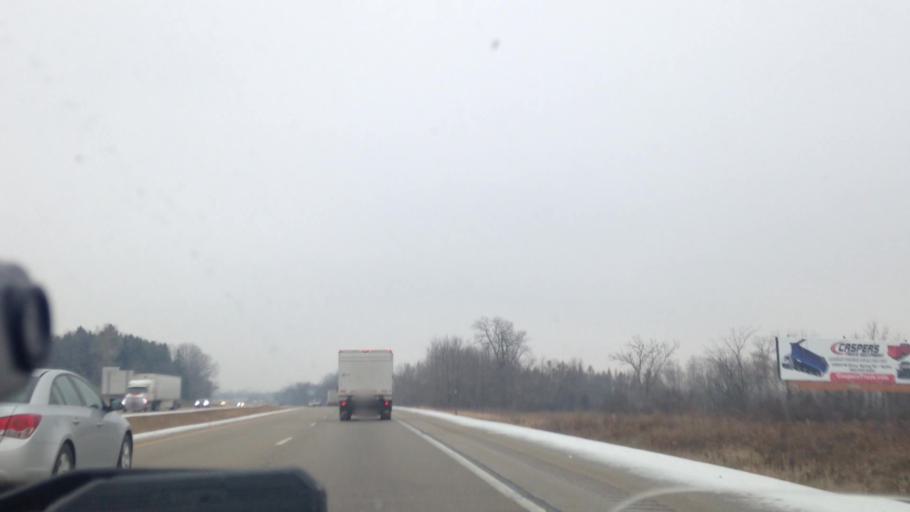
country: US
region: Wisconsin
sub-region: Washington County
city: Slinger
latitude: 43.4079
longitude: -88.3277
